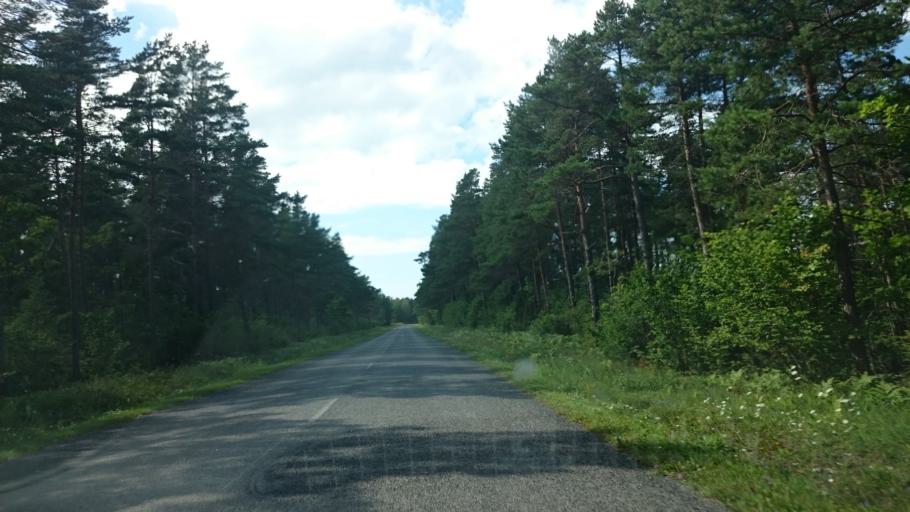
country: EE
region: Saare
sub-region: Orissaare vald
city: Orissaare
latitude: 58.5982
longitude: 22.9863
